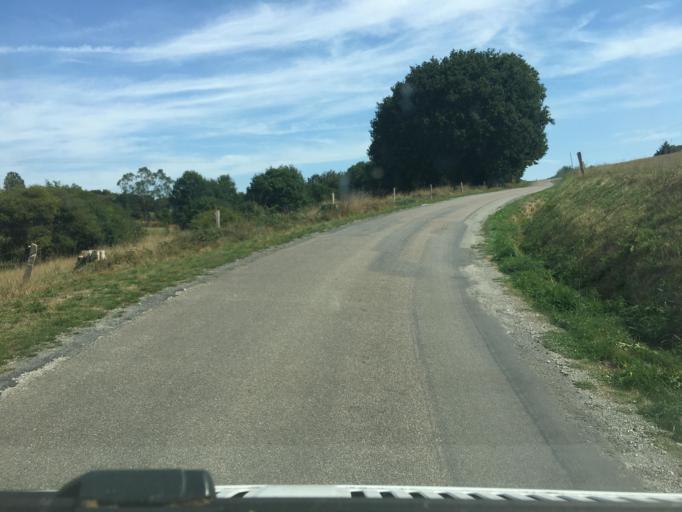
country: FR
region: Brittany
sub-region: Departement des Cotes-d'Armor
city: Mur-de-Bretagne
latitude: 48.2097
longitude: -3.0098
